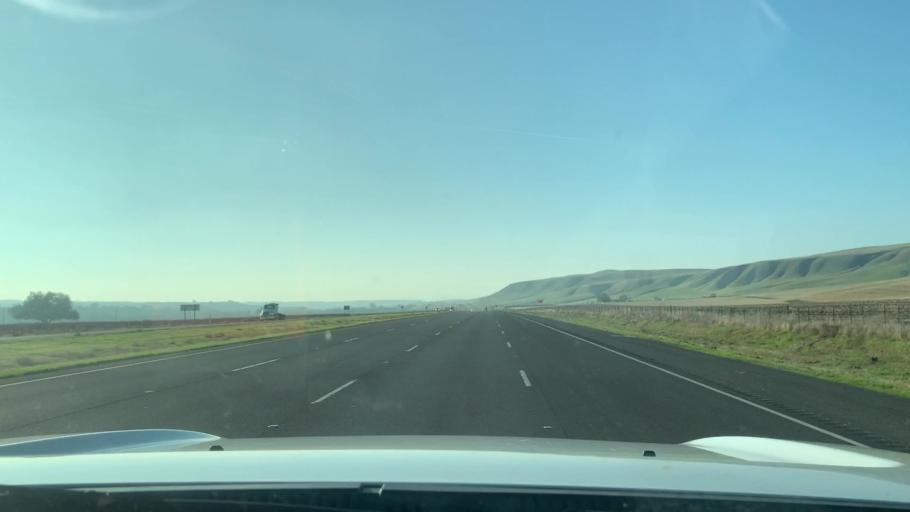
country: US
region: California
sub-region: San Luis Obispo County
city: Shandon
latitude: 35.6617
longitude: -120.4165
